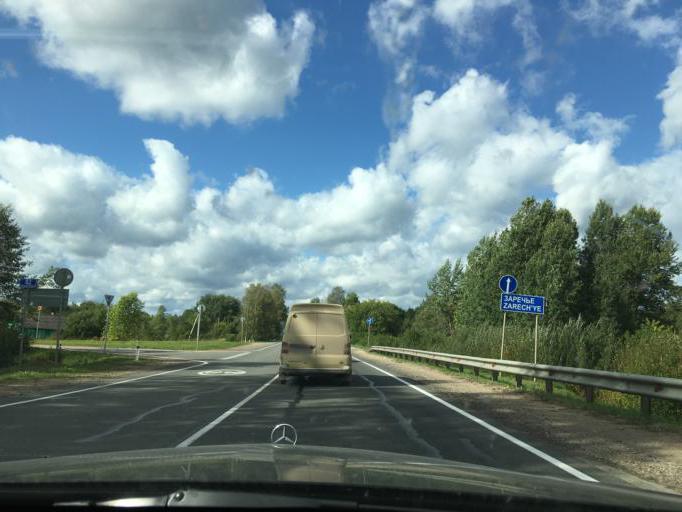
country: RU
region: Pskov
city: Pustoshka
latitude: 56.4006
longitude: 29.2322
